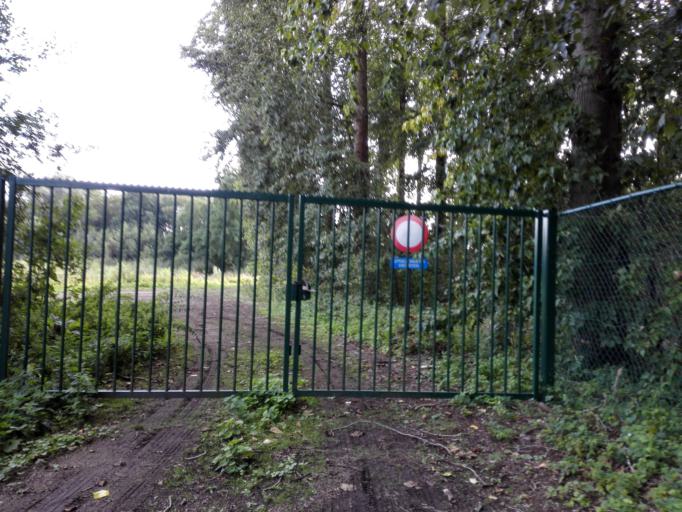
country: BE
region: Flanders
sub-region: Provincie Vlaams-Brabant
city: Oud-Heverlee
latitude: 50.8584
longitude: 4.6713
